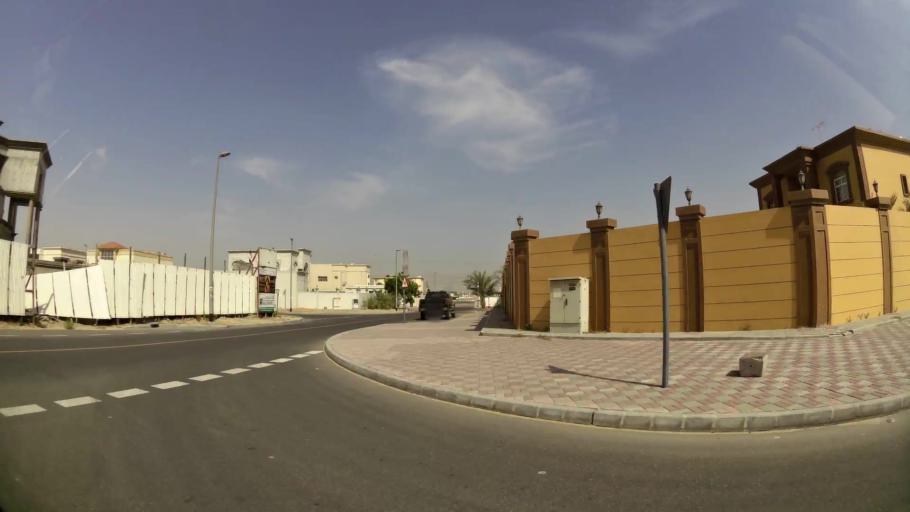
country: AE
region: Ash Shariqah
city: Sharjah
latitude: 25.2048
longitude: 55.4024
